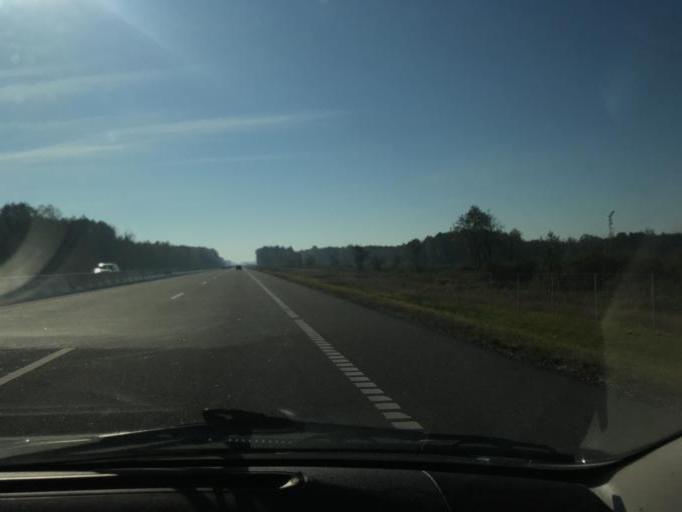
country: BY
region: Minsk
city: Slutsk
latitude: 53.2520
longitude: 27.5502
